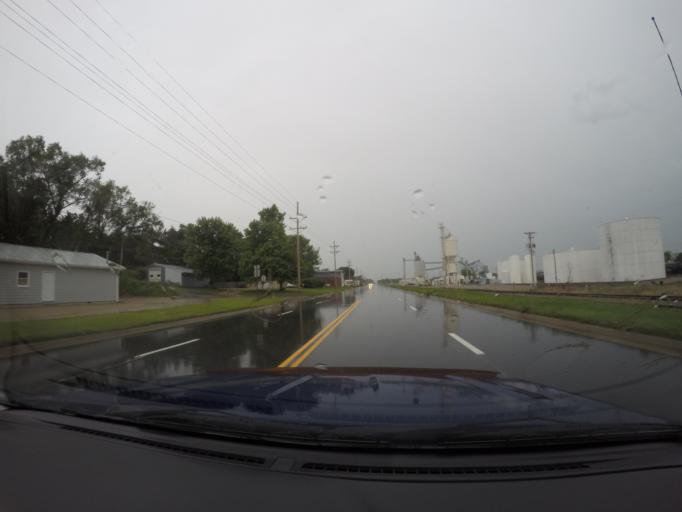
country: US
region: Kansas
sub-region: Cloud County
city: Concordia
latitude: 39.5736
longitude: -97.6698
